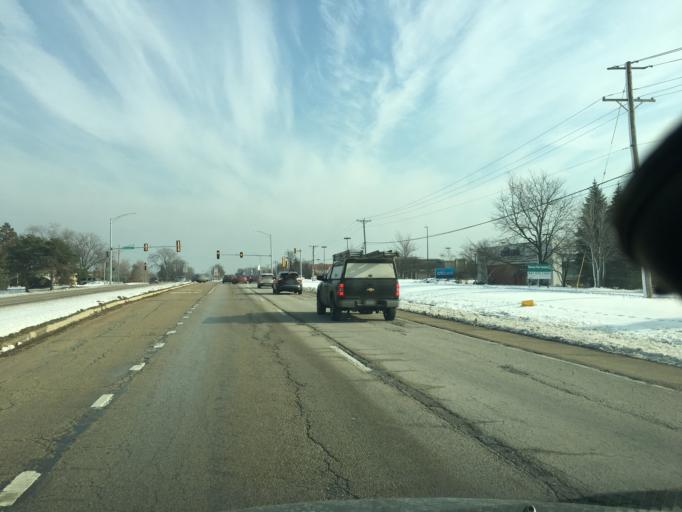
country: US
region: Illinois
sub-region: DuPage County
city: Darien
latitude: 41.7512
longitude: -88.0013
